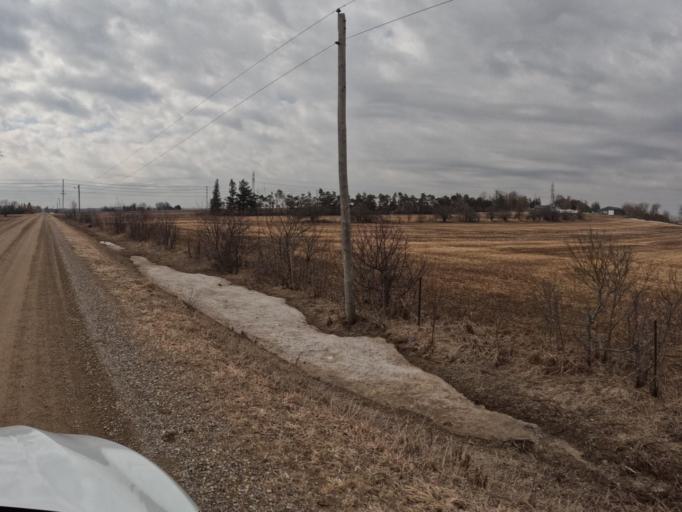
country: CA
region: Ontario
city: Orangeville
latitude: 43.9306
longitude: -80.1879
